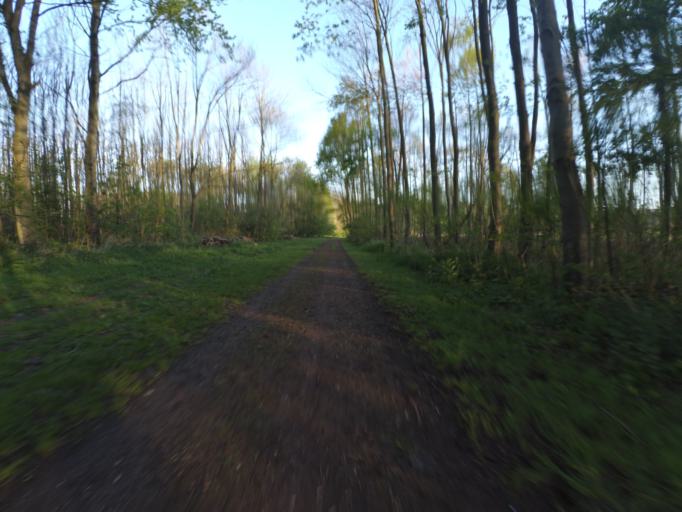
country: NL
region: Flevoland
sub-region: Gemeente Lelystad
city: Lelystad
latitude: 52.4179
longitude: 5.4939
